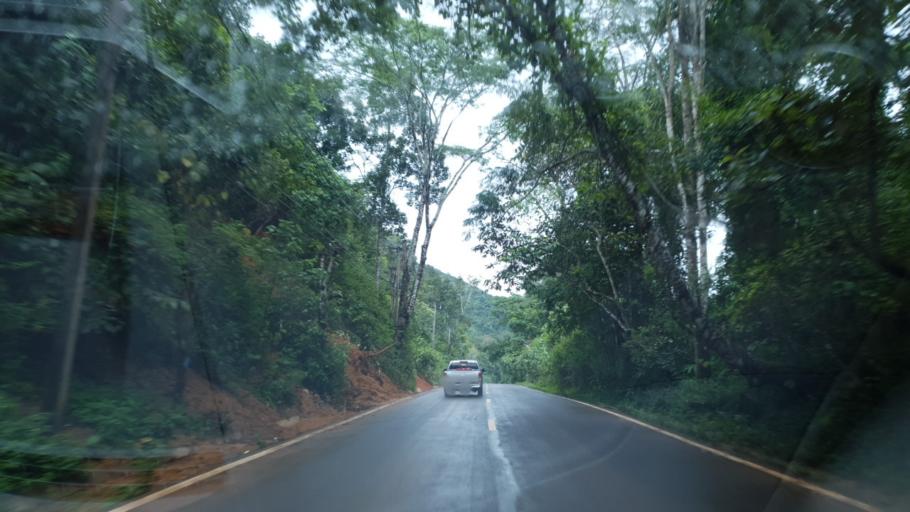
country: TH
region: Mae Hong Son
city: Ban Huai I Huak
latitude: 18.1498
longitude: 98.0964
